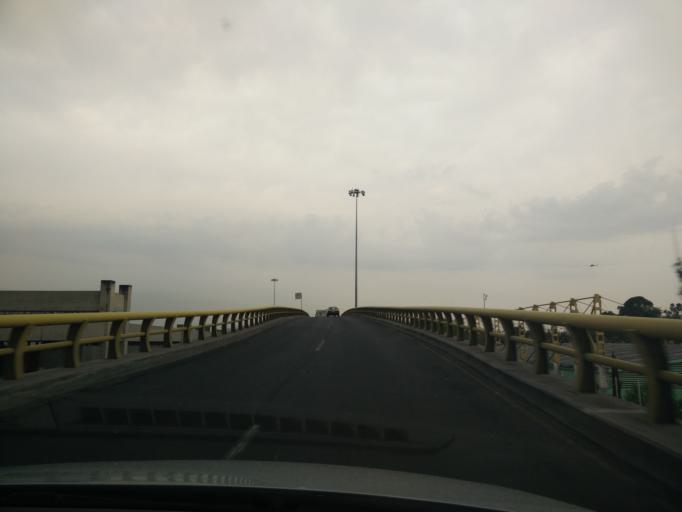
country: MX
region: Mexico City
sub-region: Iztacalco
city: Iztacalco
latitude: 19.4083
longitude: -99.0926
